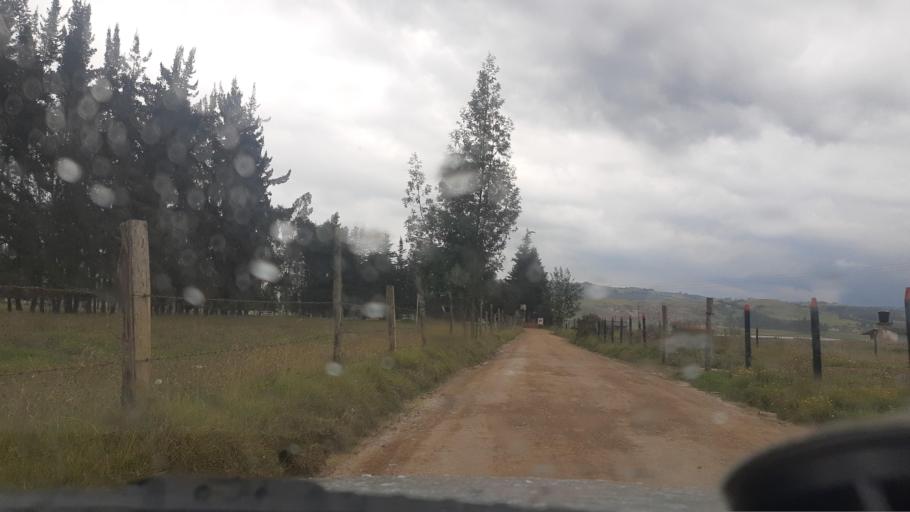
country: CO
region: Cundinamarca
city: Cucunuba
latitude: 5.1930
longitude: -73.7897
